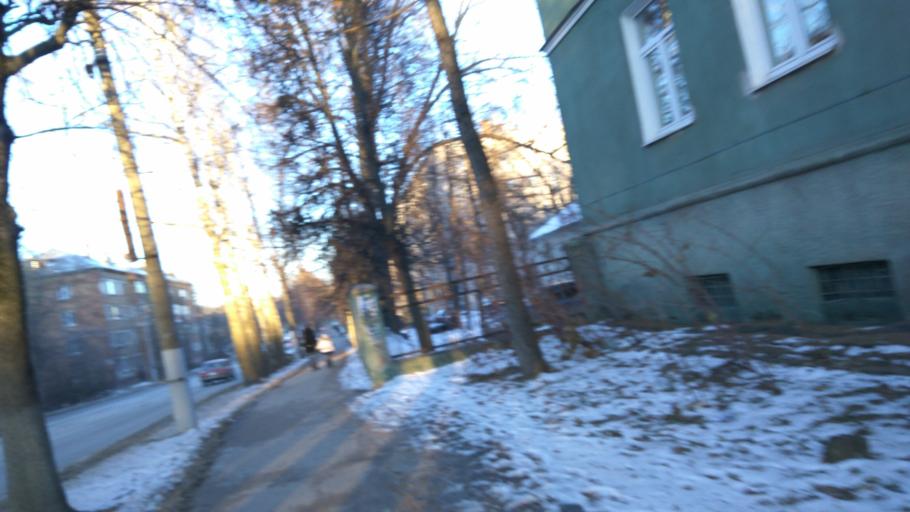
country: RU
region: Tula
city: Mendeleyevskiy
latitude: 54.1718
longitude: 37.5860
